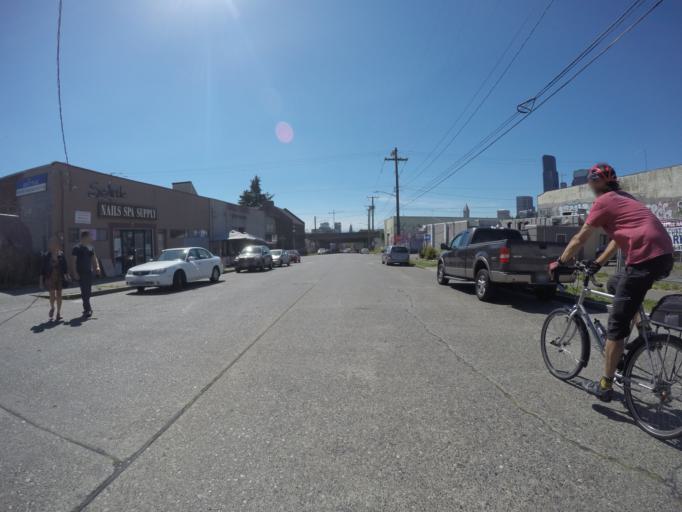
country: US
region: Washington
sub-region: King County
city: Seattle
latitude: 47.5984
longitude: -122.3191
